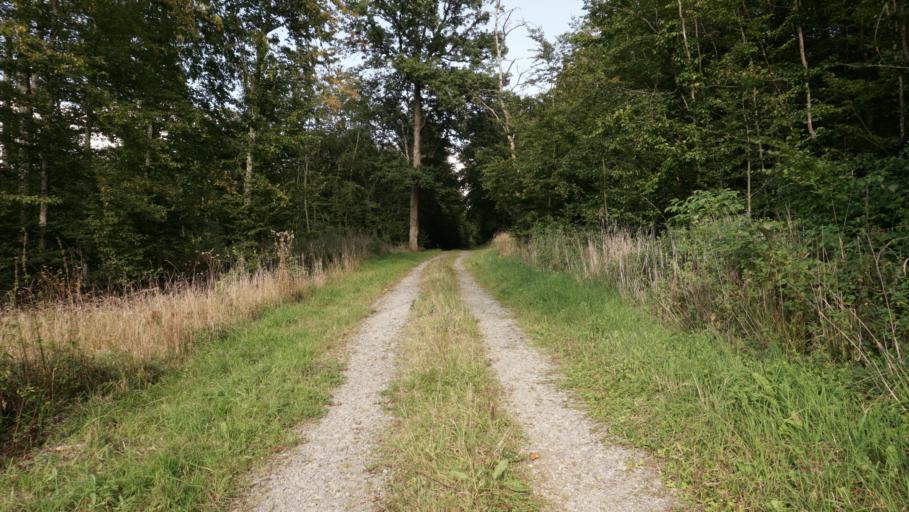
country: DE
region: Baden-Wuerttemberg
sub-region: Karlsruhe Region
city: Neckarzimmern
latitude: 49.3352
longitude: 9.1314
